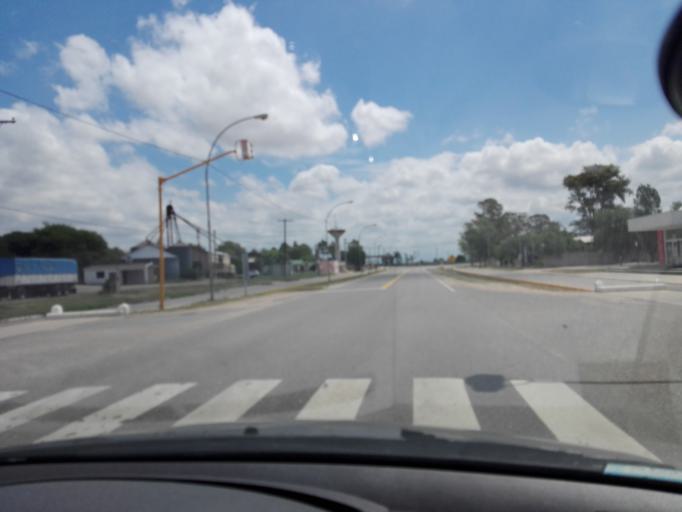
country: AR
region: Cordoba
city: Toledo
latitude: -31.6499
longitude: -64.0889
